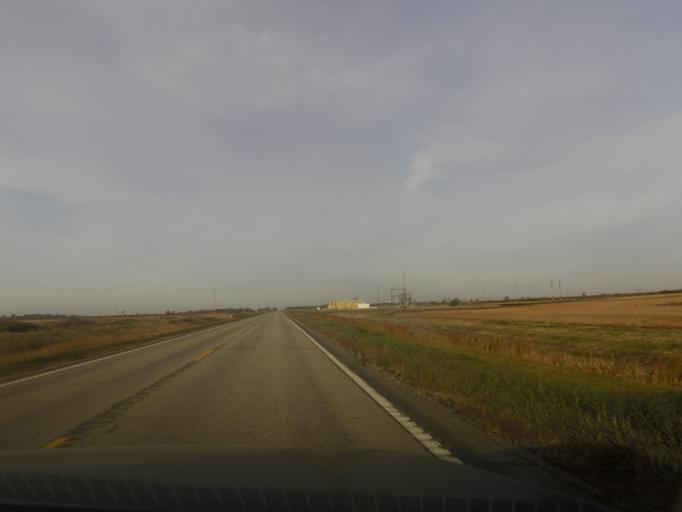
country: US
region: Minnesota
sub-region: Kittson County
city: Hallock
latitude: 48.8039
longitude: -97.2570
